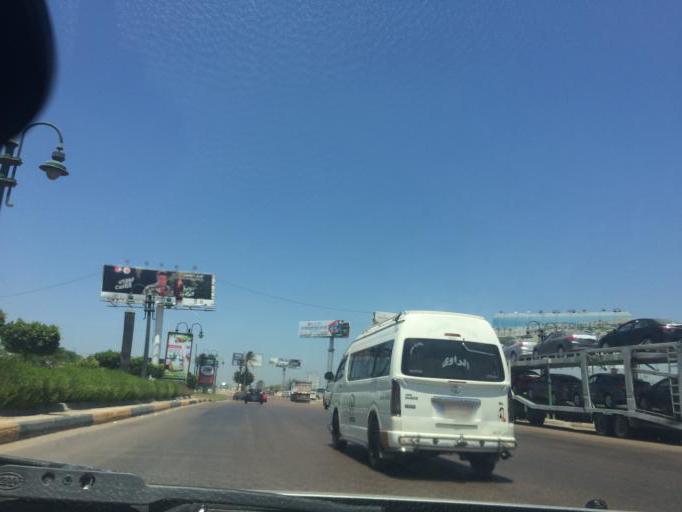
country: EG
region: Alexandria
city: Alexandria
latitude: 31.1654
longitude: 29.9354
